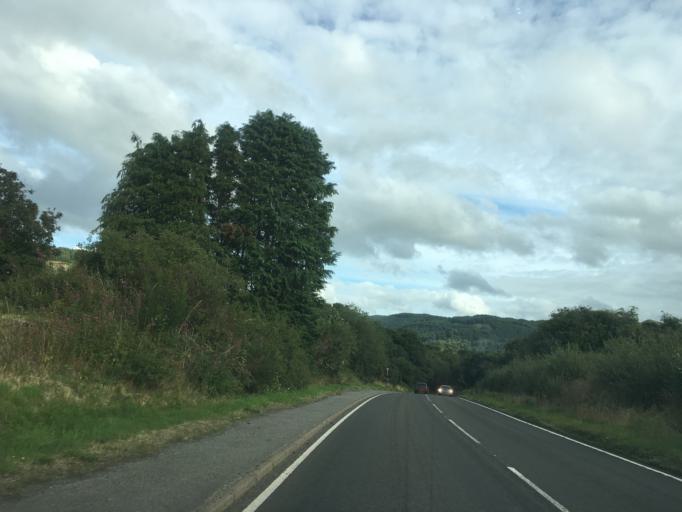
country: GB
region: Scotland
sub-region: Argyll and Bute
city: Oban
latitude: 56.3753
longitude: -5.4427
